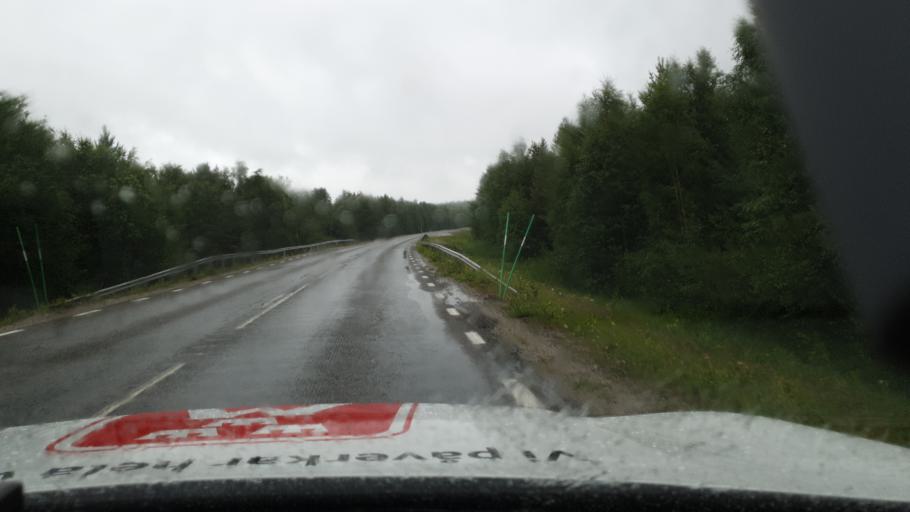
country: SE
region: Vaesterbotten
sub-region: Lycksele Kommun
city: Lycksele
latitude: 64.5250
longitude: 18.4447
